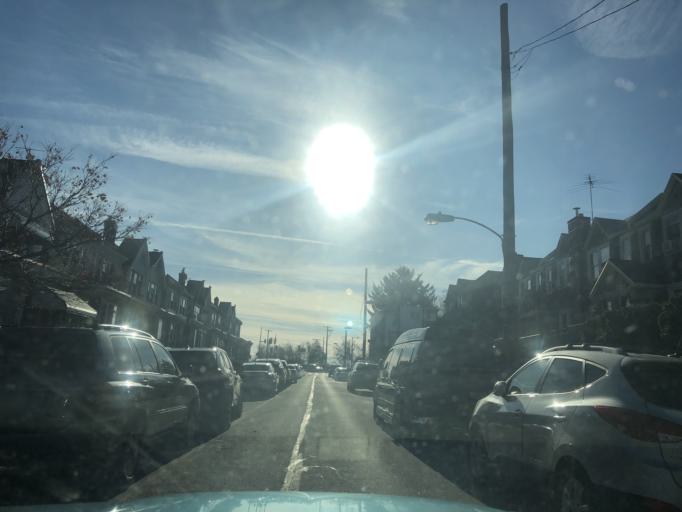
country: US
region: Pennsylvania
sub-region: Montgomery County
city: Bala-Cynwyd
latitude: 39.9859
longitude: -75.2380
